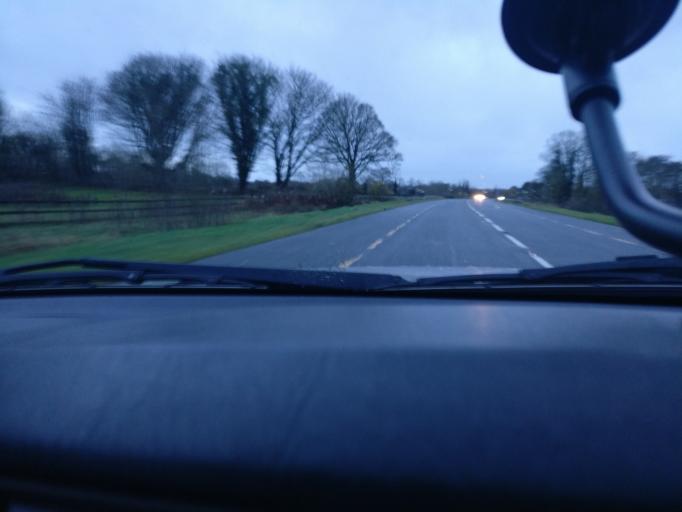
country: IE
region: Connaught
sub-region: County Galway
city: Ballinasloe
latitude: 53.2939
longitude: -8.3291
